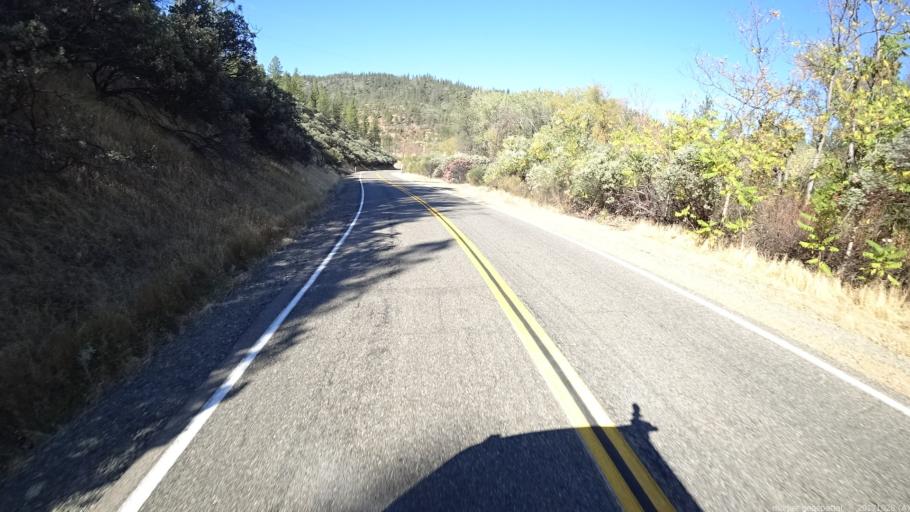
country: US
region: California
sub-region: Shasta County
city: Shasta
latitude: 40.6257
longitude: -122.4666
